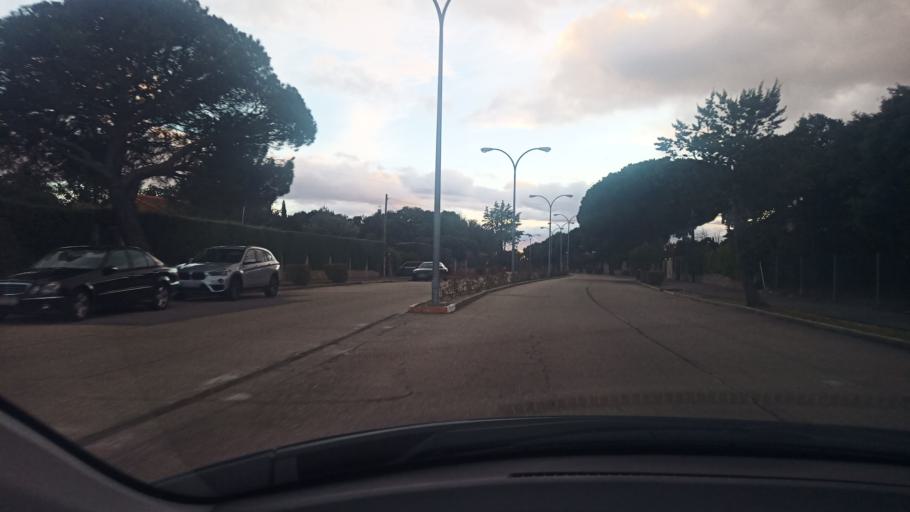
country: ES
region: Madrid
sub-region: Provincia de Madrid
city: Valdemorillo
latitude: 40.5344
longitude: -4.0927
